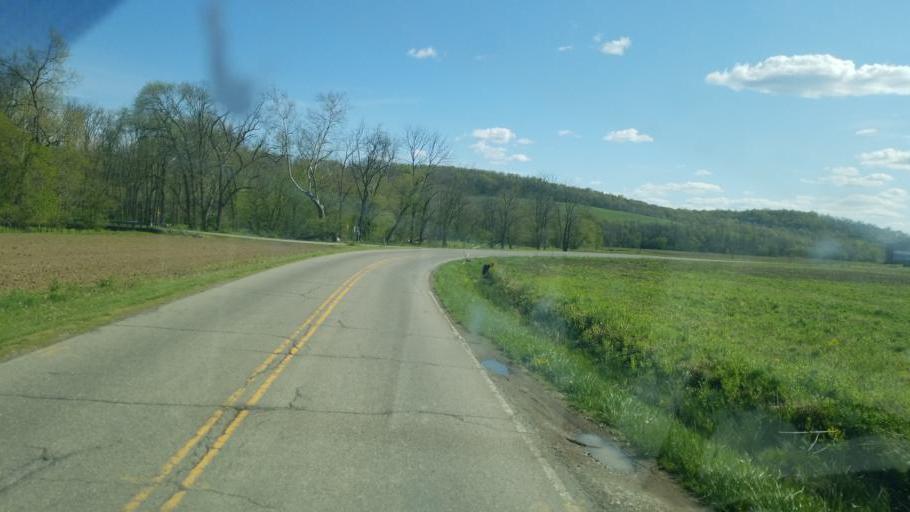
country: US
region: Ohio
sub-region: Coshocton County
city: Coshocton
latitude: 40.3685
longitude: -81.8560
